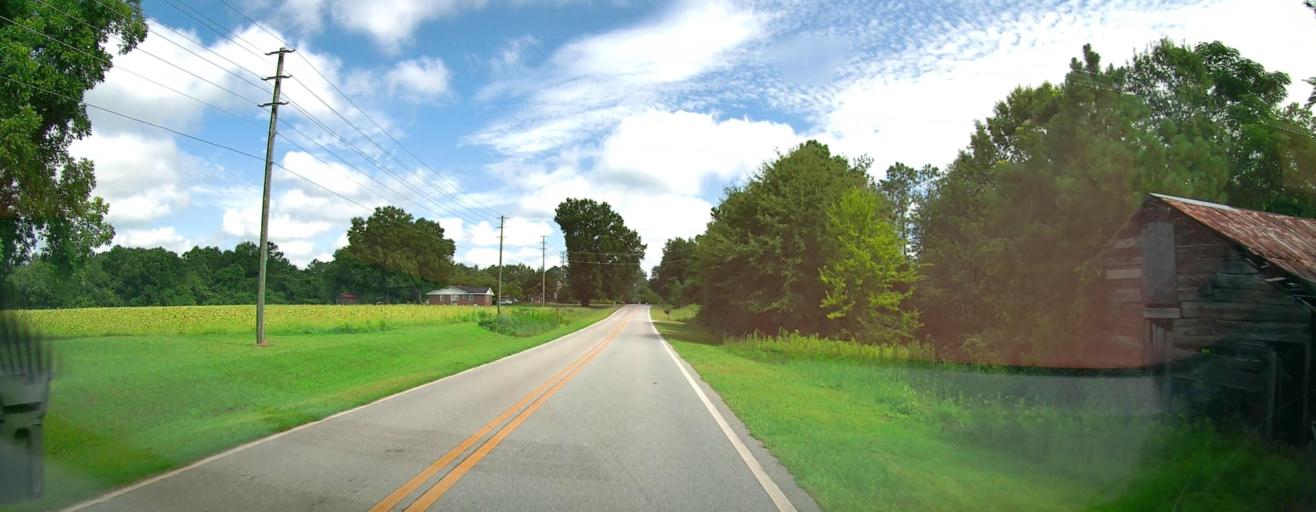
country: US
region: Georgia
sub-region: Peach County
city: Byron
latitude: 32.6139
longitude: -83.7969
